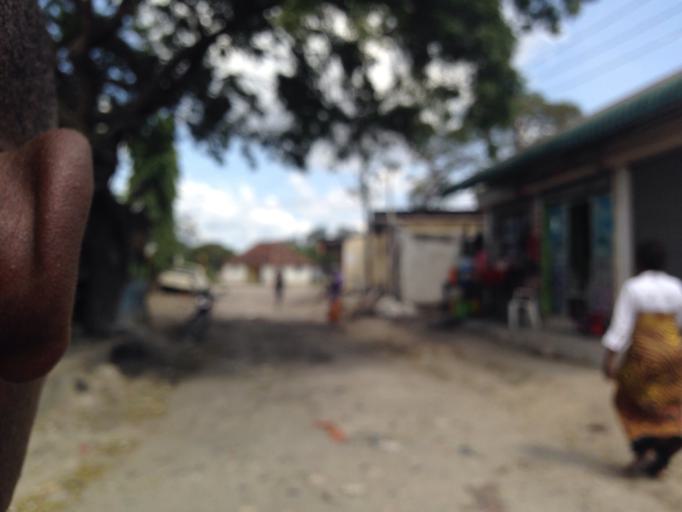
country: TZ
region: Dar es Salaam
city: Dar es Salaam
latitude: -6.8458
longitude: 39.2804
